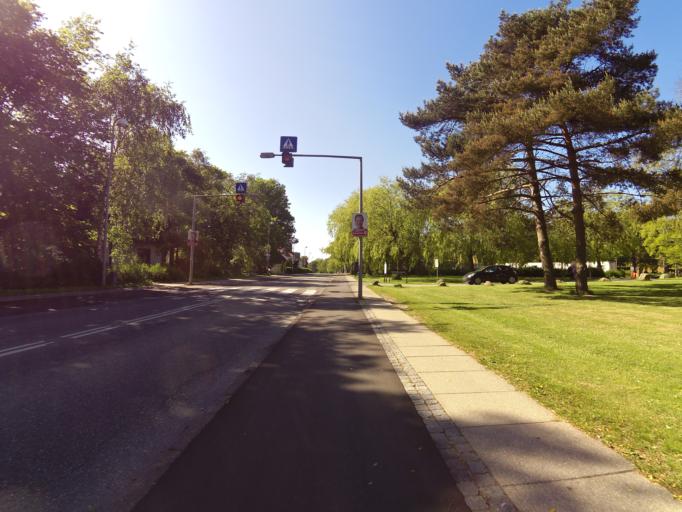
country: DK
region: Capital Region
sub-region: Gladsaxe Municipality
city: Buddinge
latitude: 55.7719
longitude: 12.4745
